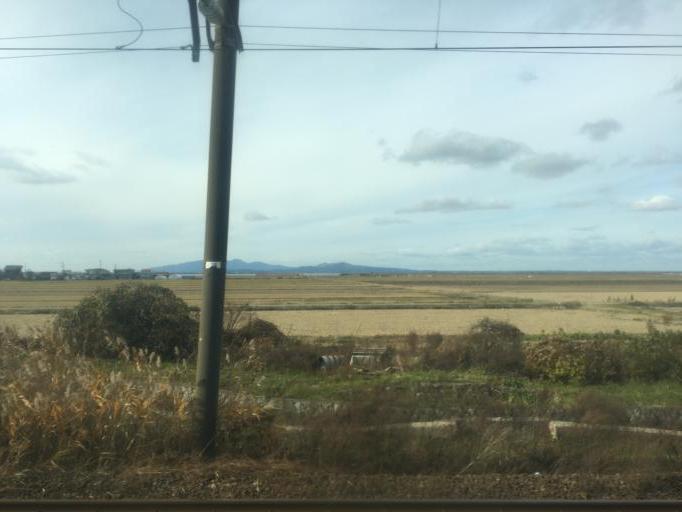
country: JP
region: Akita
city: Tenno
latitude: 39.9021
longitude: 140.0744
